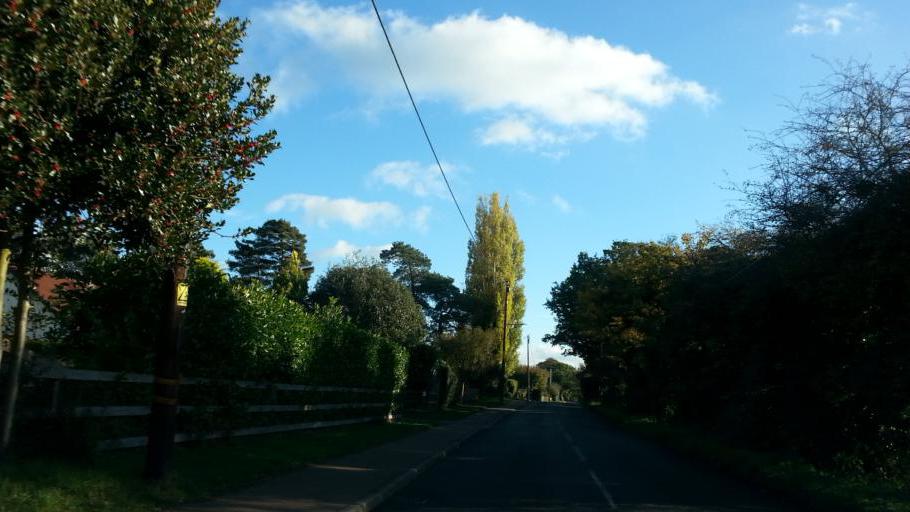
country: GB
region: England
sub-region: Suffolk
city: Great Barton
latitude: 52.2705
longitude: 0.7905
